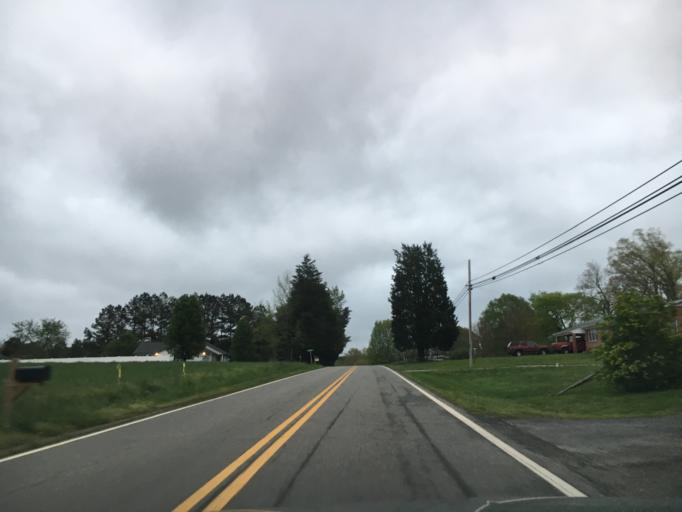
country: US
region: Virginia
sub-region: Halifax County
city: South Boston
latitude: 36.6531
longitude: -78.8742
